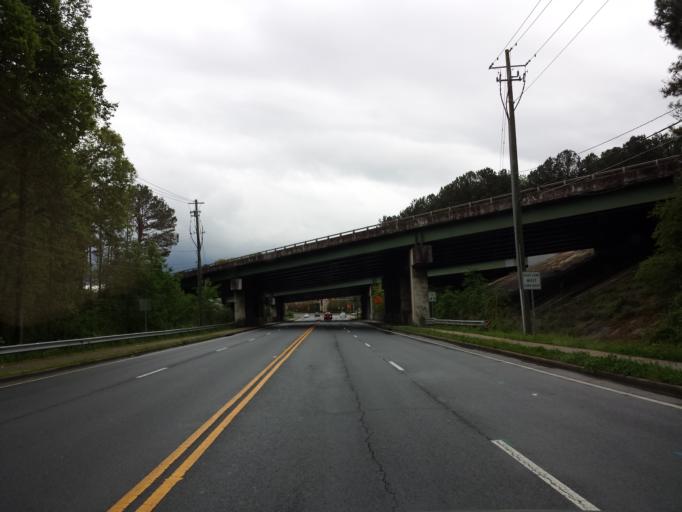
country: US
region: Georgia
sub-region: Cobb County
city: Kennesaw
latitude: 34.0447
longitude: -84.5811
